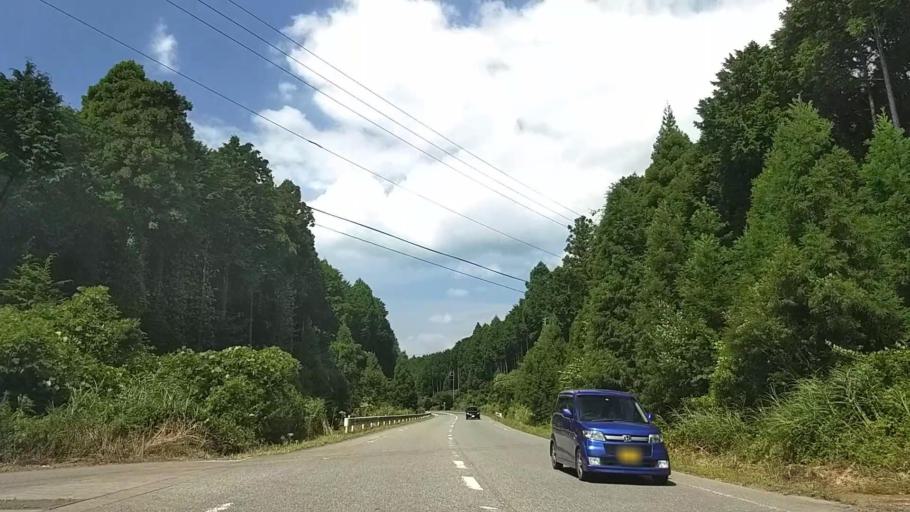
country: JP
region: Shizuoka
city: Fuji
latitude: 35.2450
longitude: 138.7162
